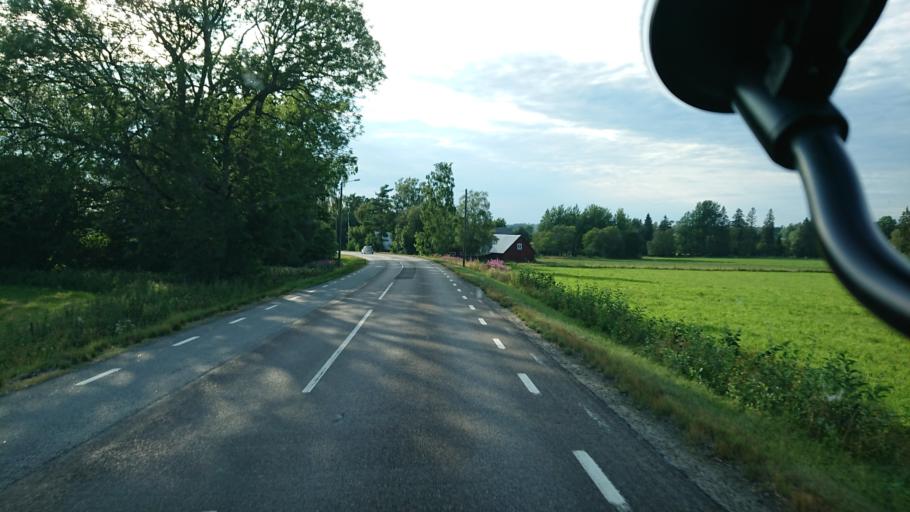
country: SE
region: Kronoberg
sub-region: Vaxjo Kommun
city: Braas
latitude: 57.0221
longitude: 15.0328
